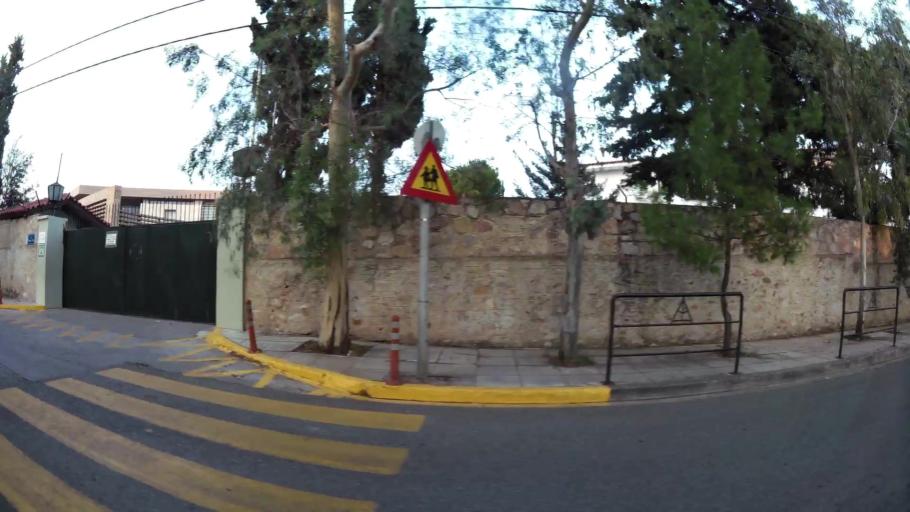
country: GR
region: Attica
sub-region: Nomarchia Athinas
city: Psychiko
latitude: 38.0173
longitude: 23.7776
